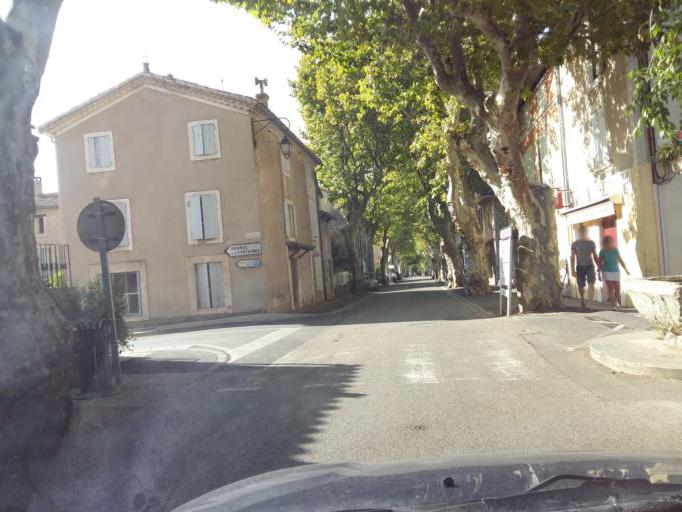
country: FR
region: Provence-Alpes-Cote d'Azur
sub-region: Departement du Vaucluse
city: Saint-Didier
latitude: 44.0058
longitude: 5.1097
